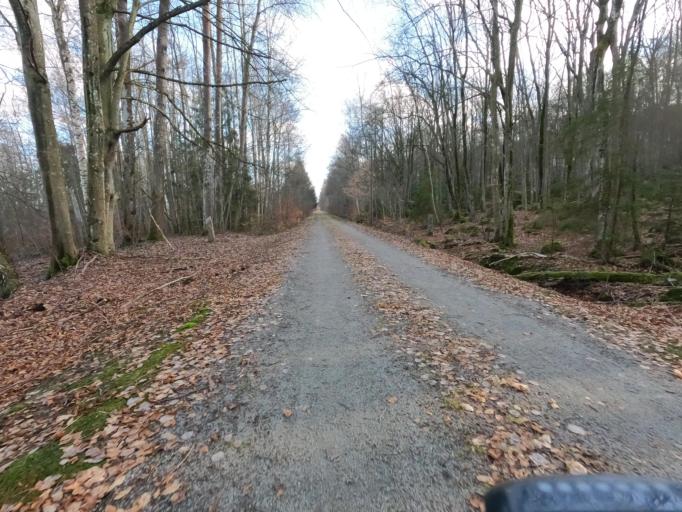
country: SE
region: Kronoberg
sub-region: Vaxjo Kommun
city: Gemla
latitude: 56.6752
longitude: 14.6162
